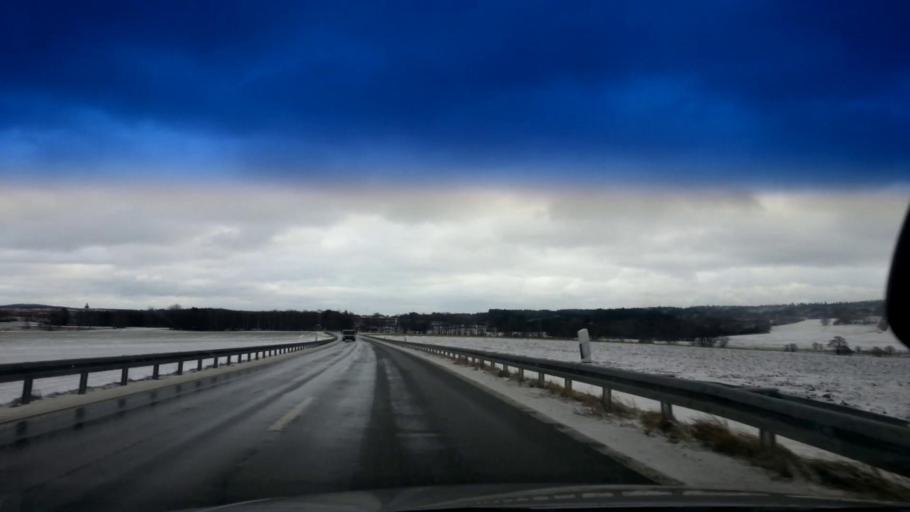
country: DE
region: Bavaria
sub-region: Upper Franconia
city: Weissenstadt
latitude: 50.0948
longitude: 11.8527
